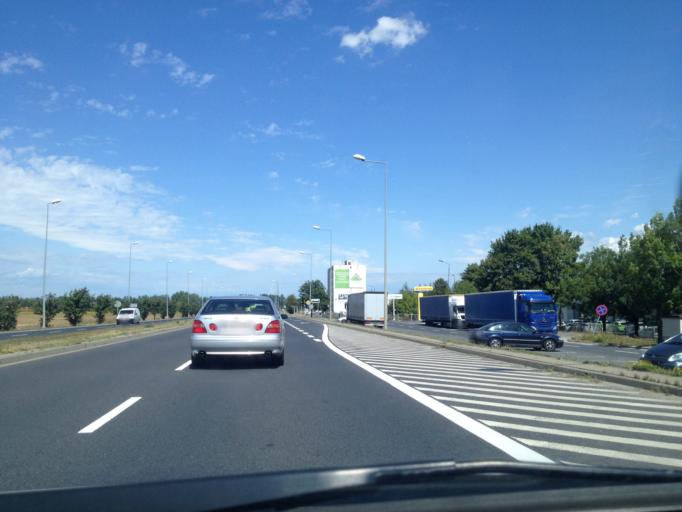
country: PL
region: Lower Silesian Voivodeship
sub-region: Legnica
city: Legnica
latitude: 51.1688
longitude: 16.1727
